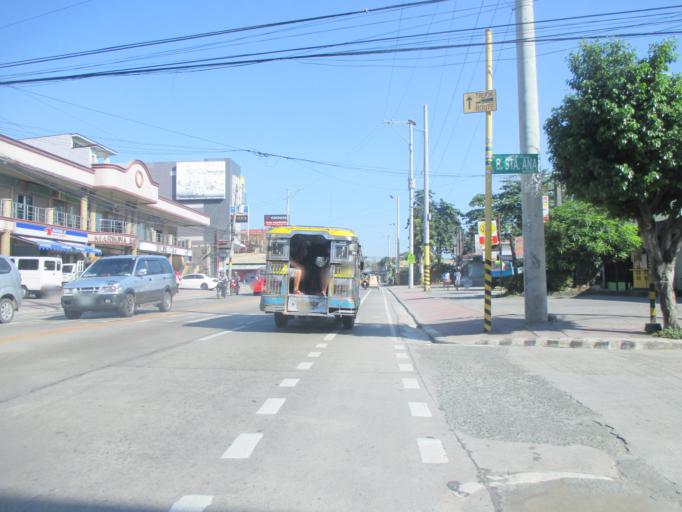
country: PH
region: Metro Manila
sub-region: Marikina
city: Calumpang
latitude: 14.6243
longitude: 121.1024
